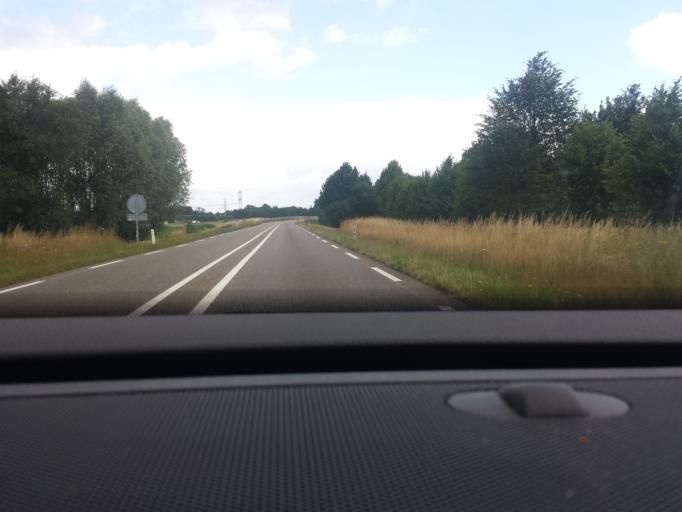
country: NL
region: Gelderland
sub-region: Gemeente Lochem
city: Lochem
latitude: 52.1615
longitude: 6.3905
